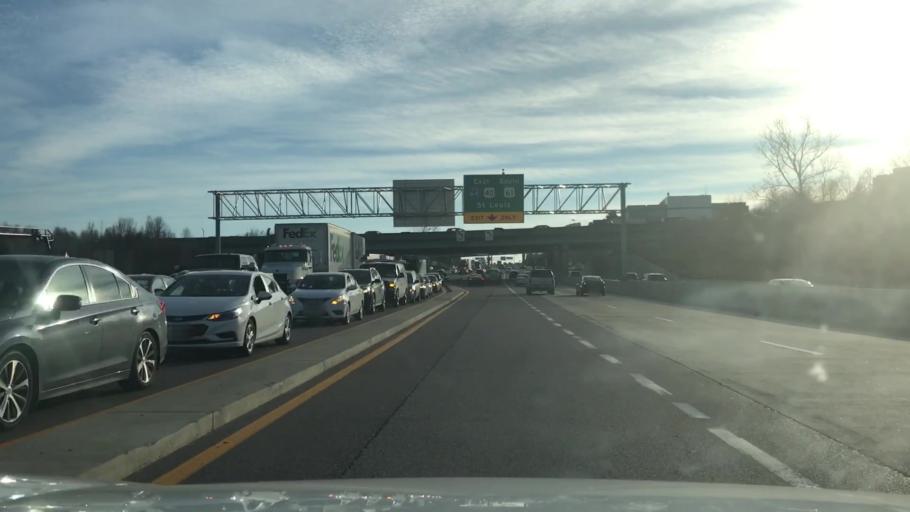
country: US
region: Missouri
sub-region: Saint Louis County
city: Manchester
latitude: 38.6437
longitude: -90.5100
